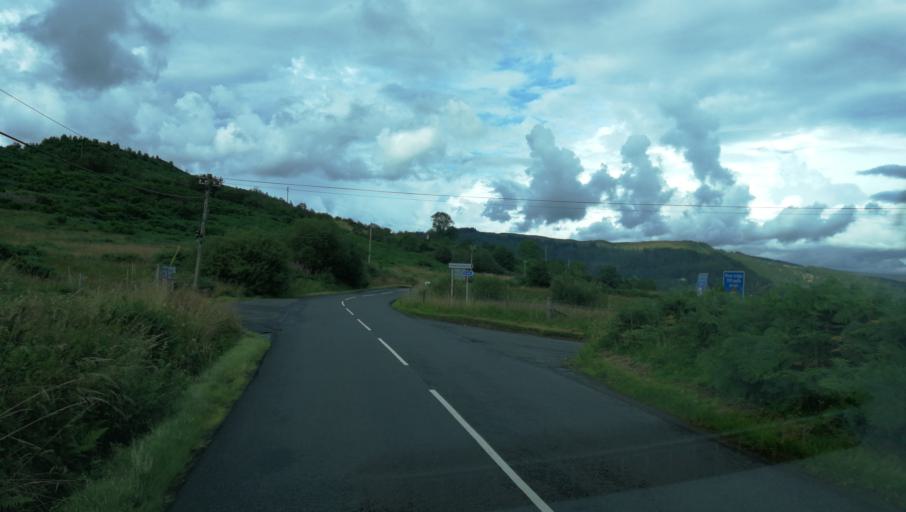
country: GB
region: Scotland
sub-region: Stirling
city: Callander
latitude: 56.2379
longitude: -4.2564
